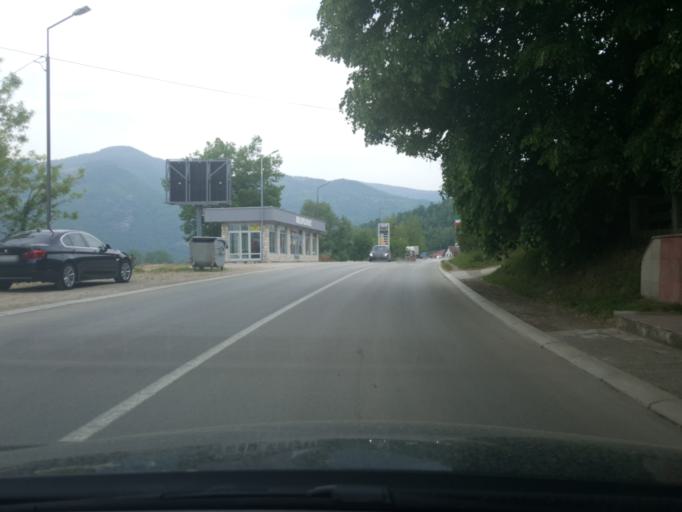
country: RS
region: Central Serbia
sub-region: Zlatiborski Okrug
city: Bajina Basta
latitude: 43.9849
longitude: 19.5685
